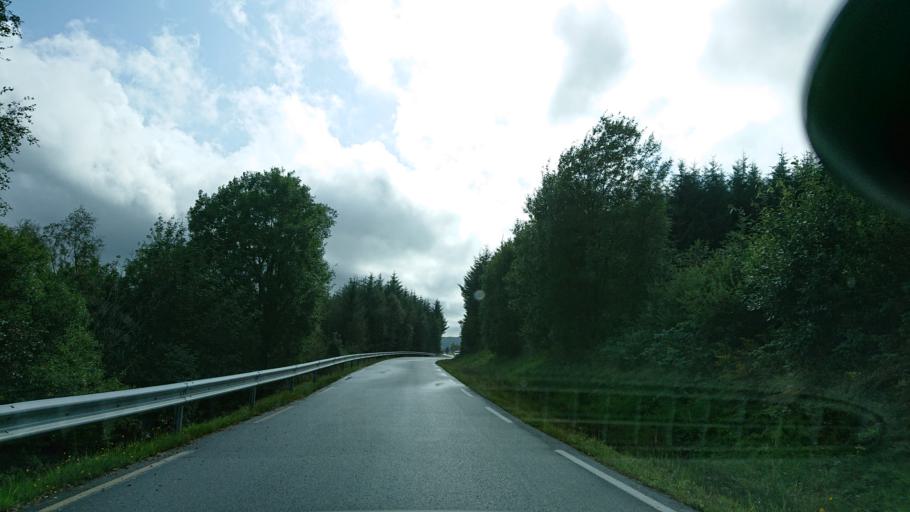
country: NO
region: Rogaland
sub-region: Gjesdal
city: Algard
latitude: 58.6901
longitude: 5.8771
